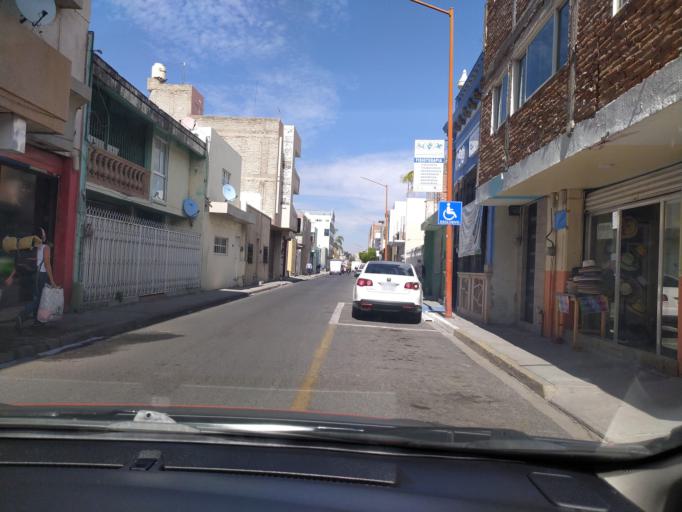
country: LA
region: Oudomxai
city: Muang La
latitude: 21.0209
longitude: 101.8563
